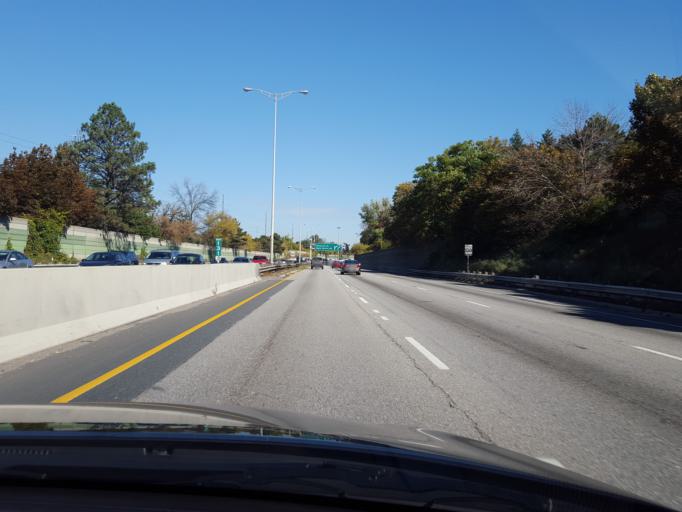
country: CA
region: Ontario
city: Mississauga
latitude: 43.5601
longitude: -79.6074
